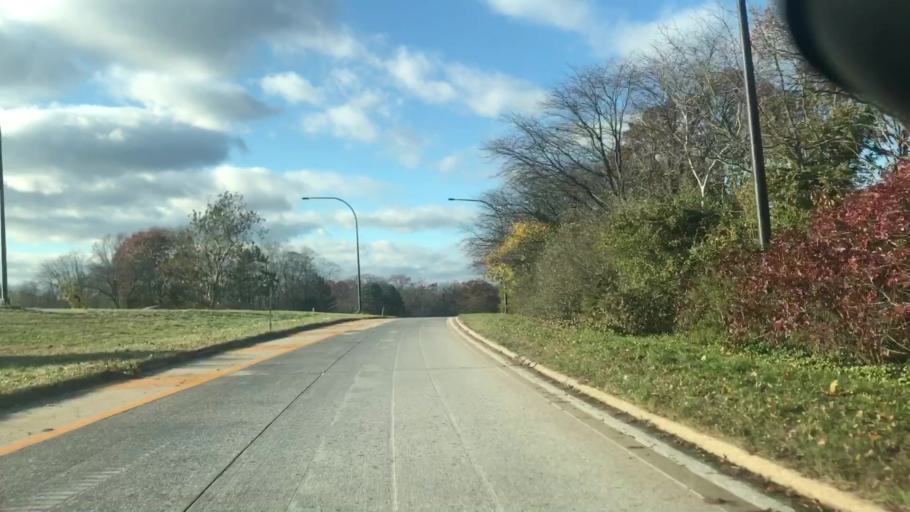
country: US
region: New York
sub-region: Nassau County
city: North Wantagh
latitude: 40.6999
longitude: -73.5186
